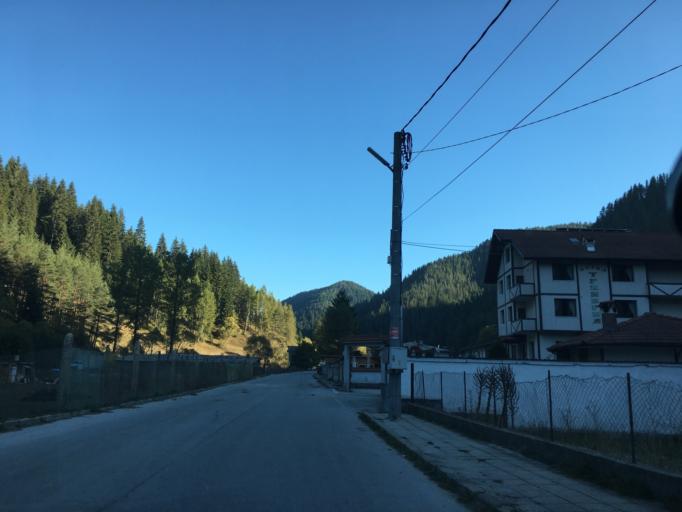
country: BG
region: Smolyan
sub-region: Obshtina Borino
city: Borino
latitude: 41.5932
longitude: 24.3811
